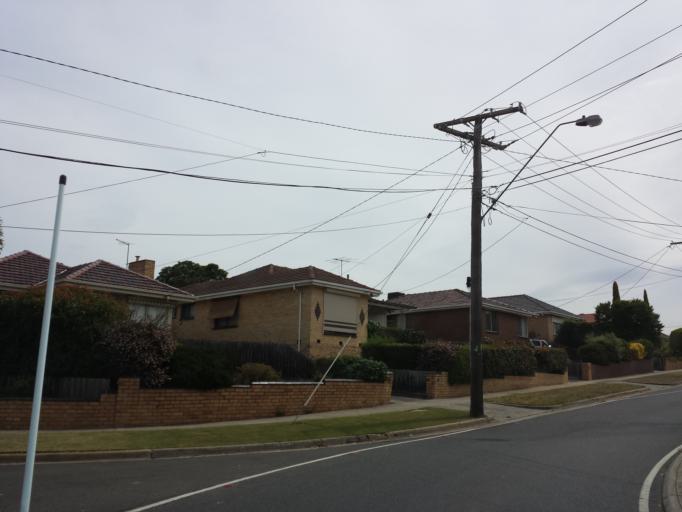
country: AU
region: Victoria
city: Highett
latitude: -37.9494
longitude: 145.0507
